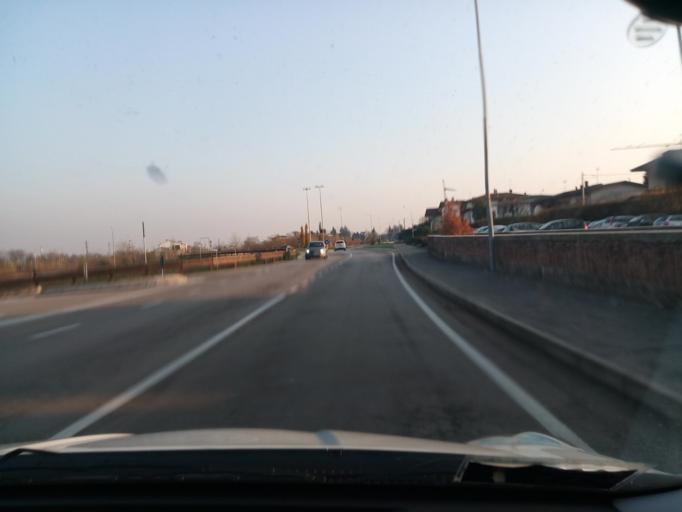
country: IT
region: Veneto
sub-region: Provincia di Vicenza
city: Schio
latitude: 45.7054
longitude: 11.3610
